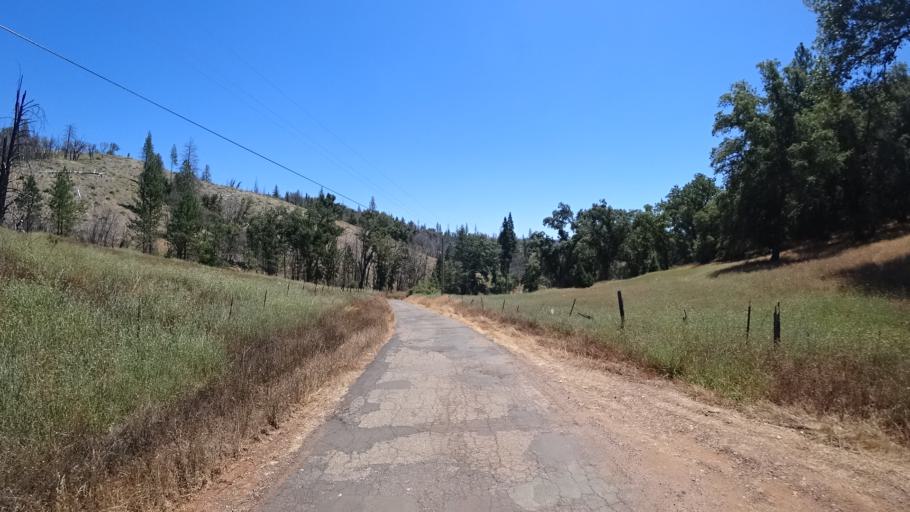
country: US
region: California
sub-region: Calaveras County
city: Mountain Ranch
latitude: 38.2671
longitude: -120.5853
